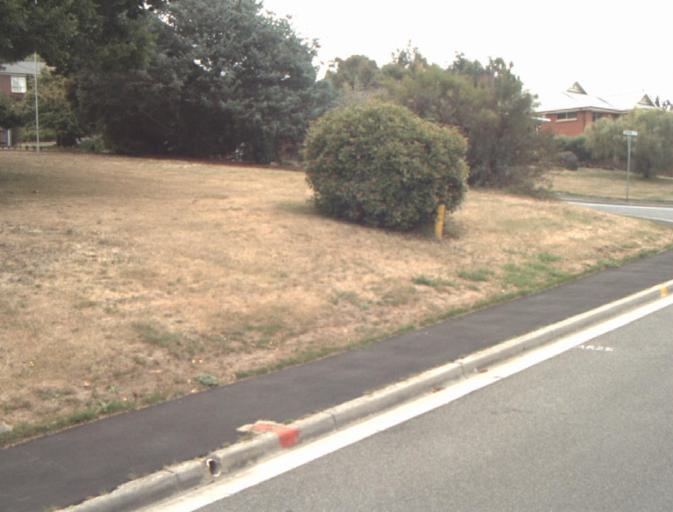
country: AU
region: Tasmania
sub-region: Launceston
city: Newstead
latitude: -41.4631
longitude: 147.1835
